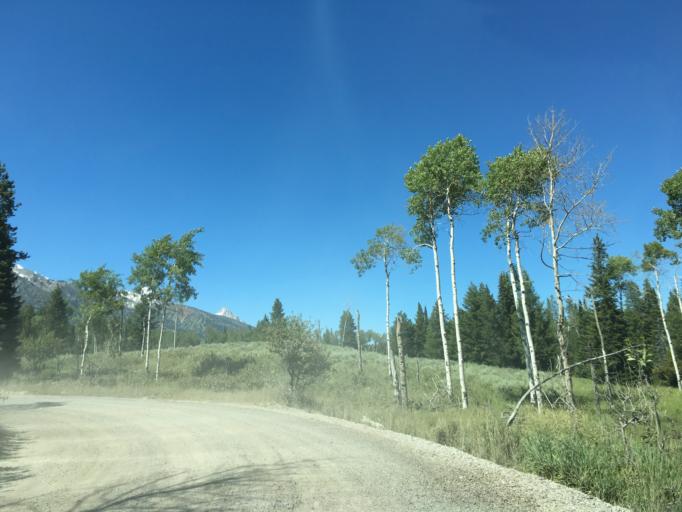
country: US
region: Wyoming
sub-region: Teton County
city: Moose Wilson Road
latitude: 43.6100
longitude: -110.7920
